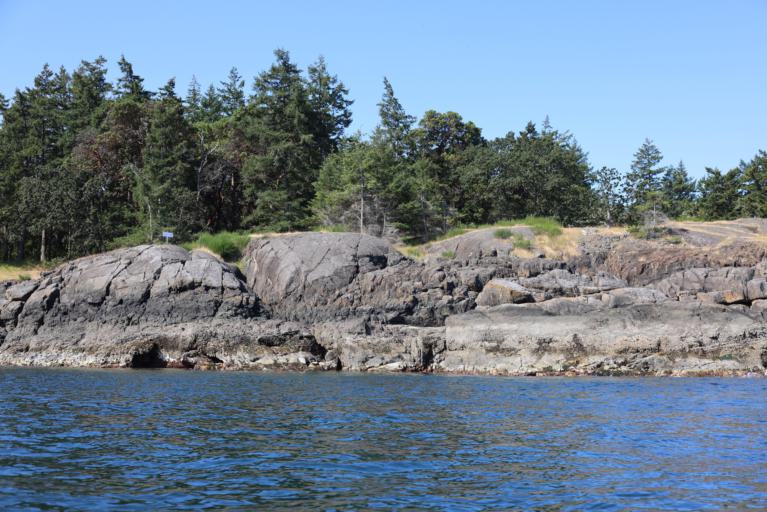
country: CA
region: British Columbia
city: Colwood
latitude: 48.3903
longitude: -123.4777
